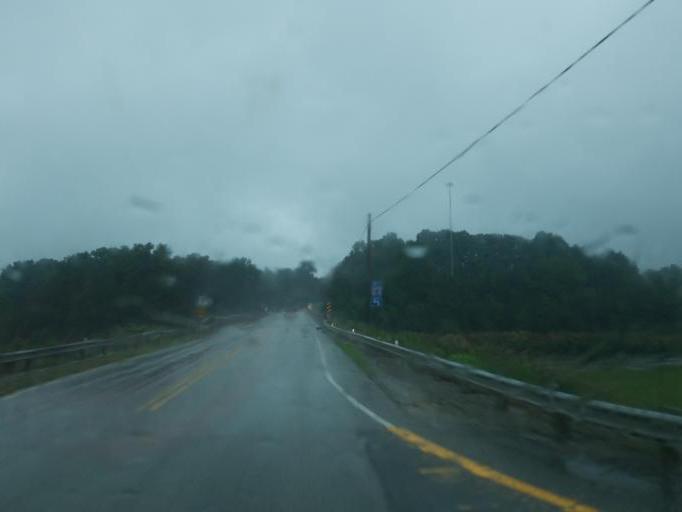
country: US
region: Kentucky
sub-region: Carter County
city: Olive Hill
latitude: 38.3305
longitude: -83.2089
